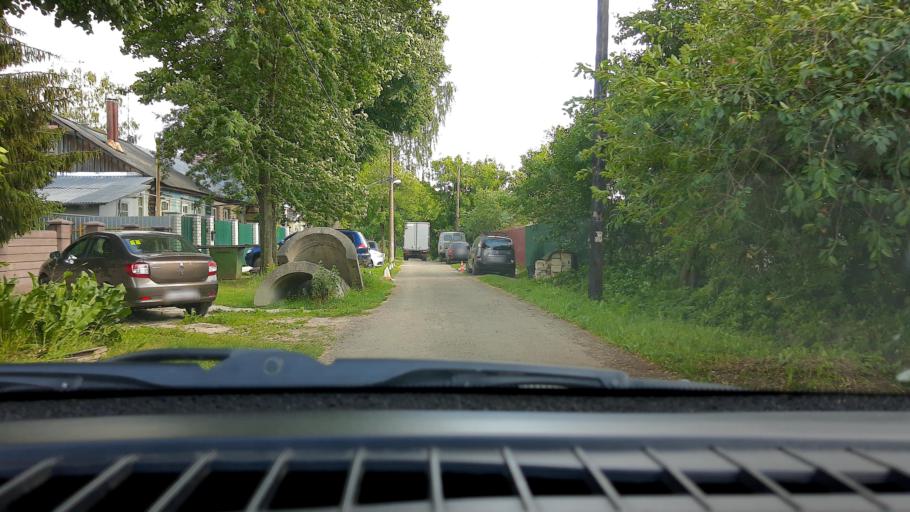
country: RU
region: Nizjnij Novgorod
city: Burevestnik
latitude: 56.1744
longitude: 43.7716
